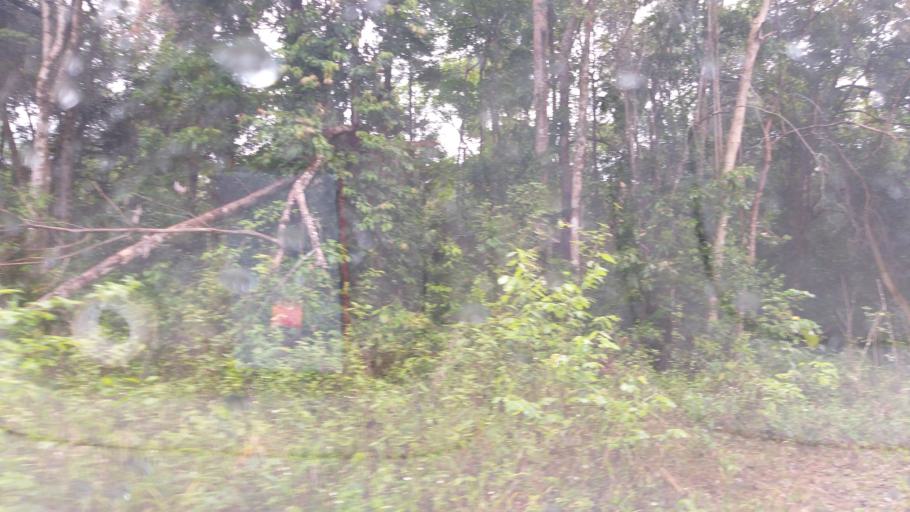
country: TH
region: Trat
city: Ko Chang Tai
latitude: 11.9817
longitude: 102.3246
